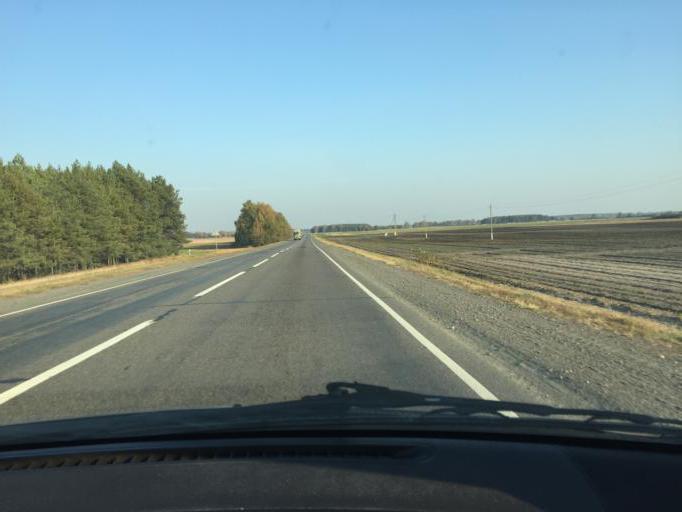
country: BY
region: Brest
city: Davyd-Haradok
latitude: 52.2436
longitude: 27.1610
